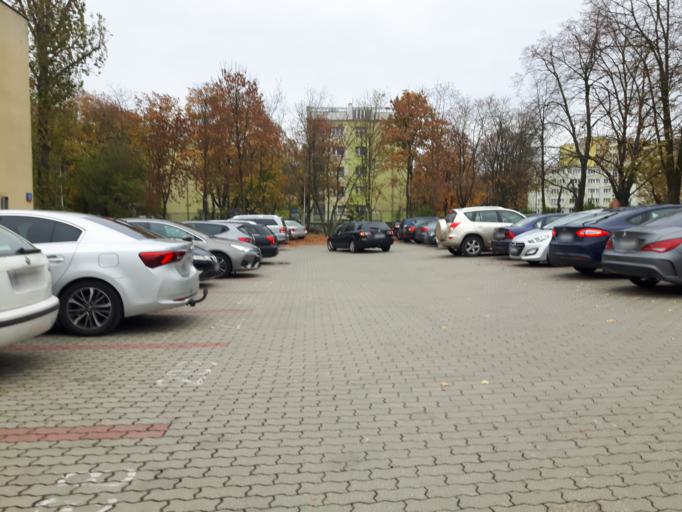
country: PL
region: Masovian Voivodeship
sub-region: Warszawa
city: Praga Poludnie
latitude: 52.2503
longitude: 21.0917
